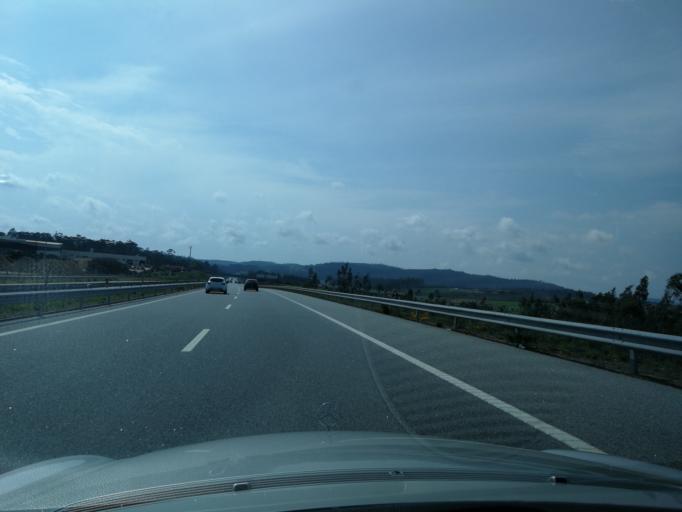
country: PT
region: Braga
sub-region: Vila Nova de Famalicao
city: Ribeirao
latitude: 41.3923
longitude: -8.6078
